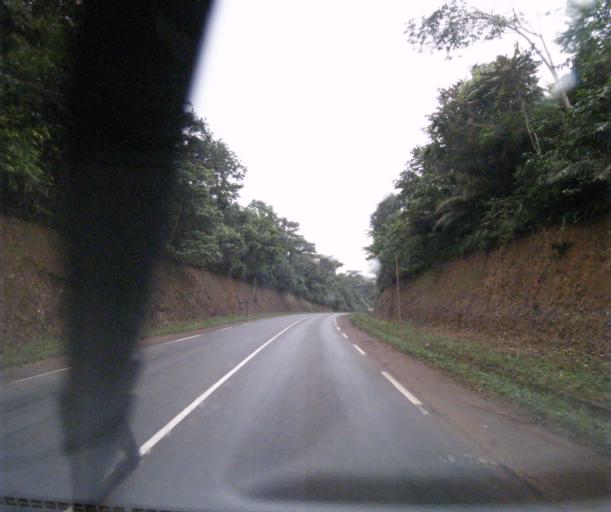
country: CM
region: Centre
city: Mbankomo
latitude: 3.7665
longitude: 11.2062
